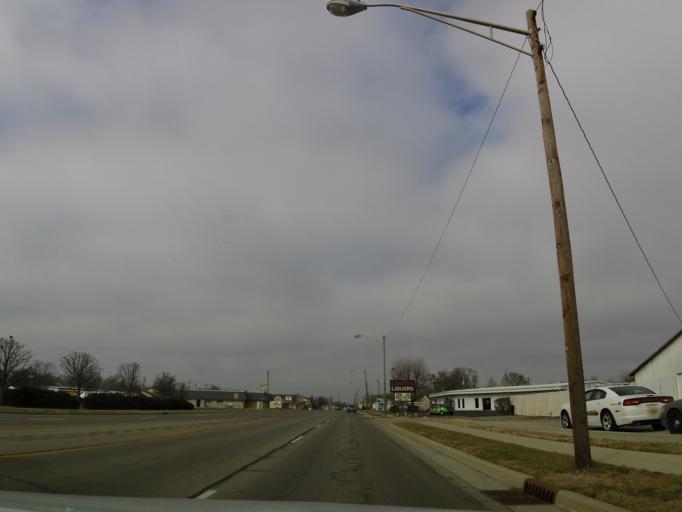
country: US
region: Indiana
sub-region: Bartholomew County
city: Columbus
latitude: 39.1942
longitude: -85.8964
